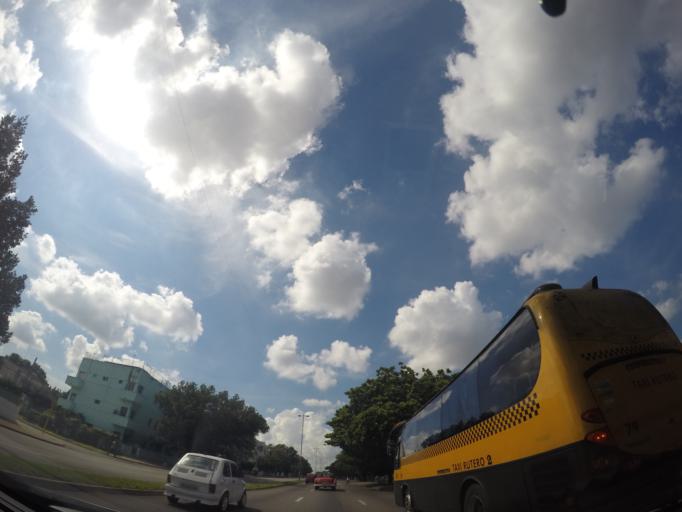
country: CU
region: La Habana
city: Havana
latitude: 23.1183
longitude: -82.4170
